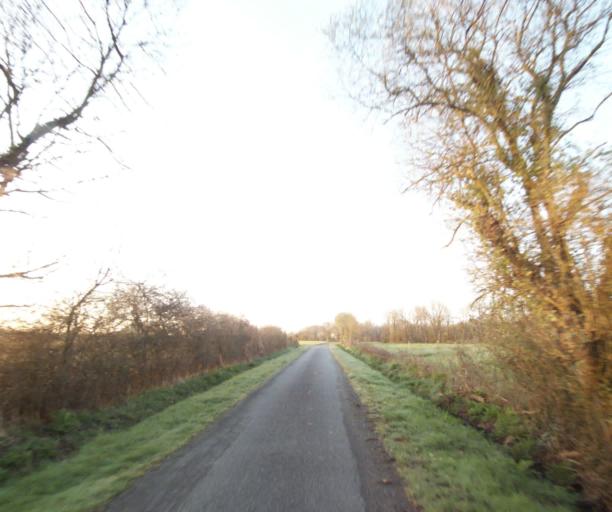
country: FR
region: Pays de la Loire
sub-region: Departement de la Loire-Atlantique
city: Quilly
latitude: 47.4409
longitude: -1.9042
